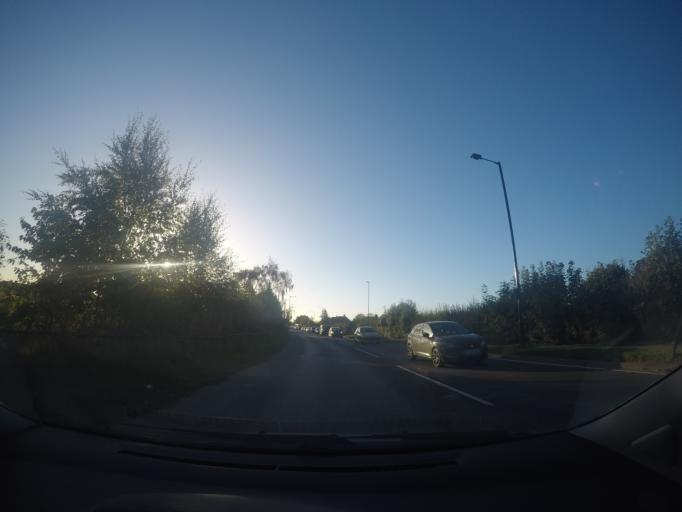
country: GB
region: England
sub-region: City of York
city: Fulford
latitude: 53.9298
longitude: -1.0711
